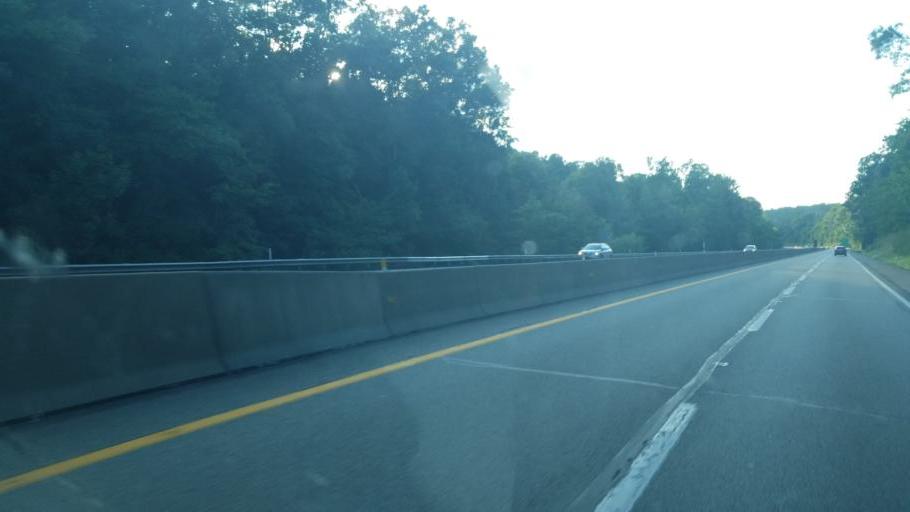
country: US
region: Pennsylvania
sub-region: Beaver County
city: West Mayfield
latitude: 40.8009
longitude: -80.2966
